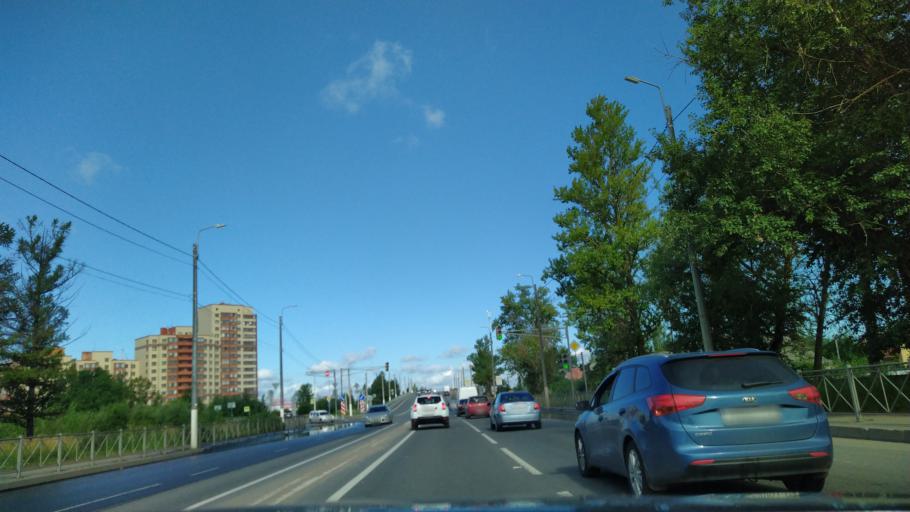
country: RU
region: Leningrad
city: Tosno
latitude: 59.5484
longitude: 30.8636
